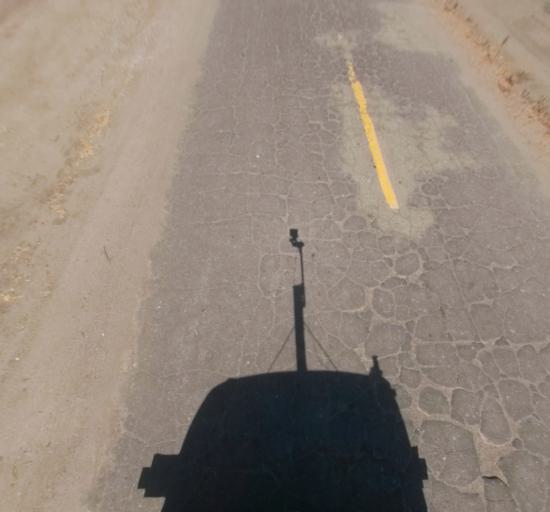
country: US
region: California
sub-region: Madera County
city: Chowchilla
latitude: 37.0327
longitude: -120.3089
